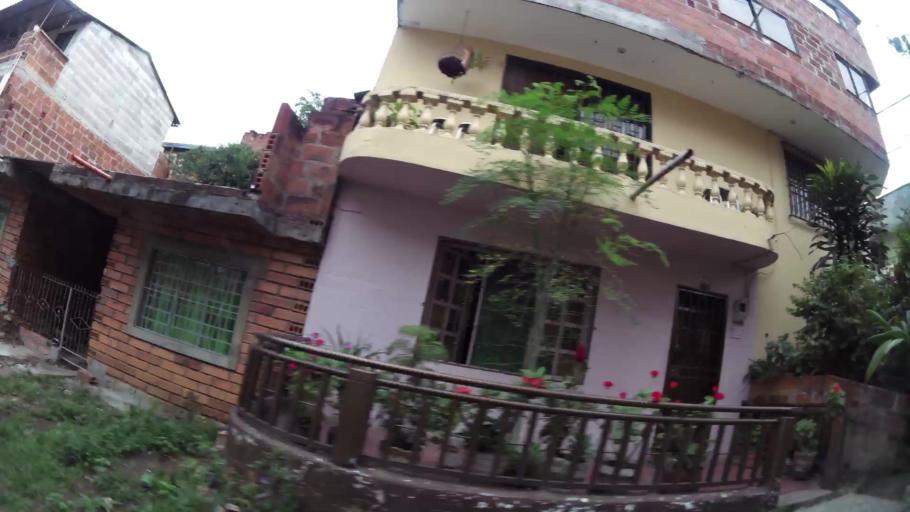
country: CO
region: Antioquia
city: Medellin
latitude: 6.2903
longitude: -75.5595
